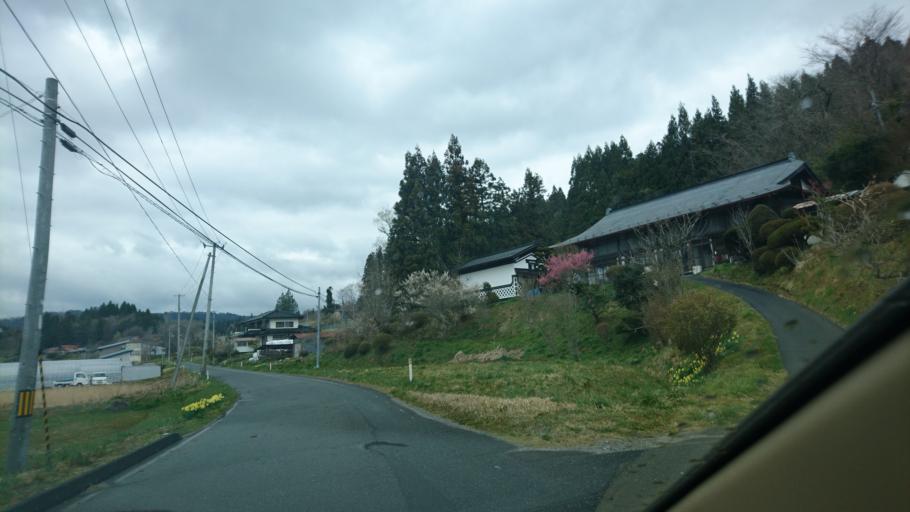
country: JP
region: Iwate
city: Ichinoseki
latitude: 38.9434
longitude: 141.3243
